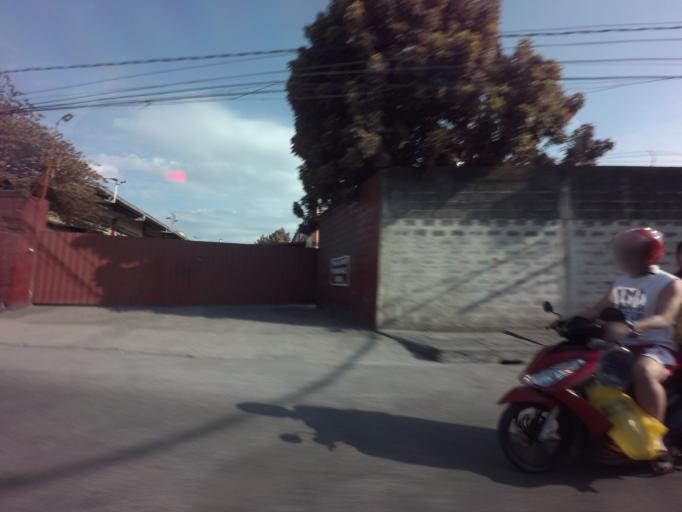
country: PH
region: Calabarzon
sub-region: Province of Rizal
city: Taguig
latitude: 14.4792
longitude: 121.0512
